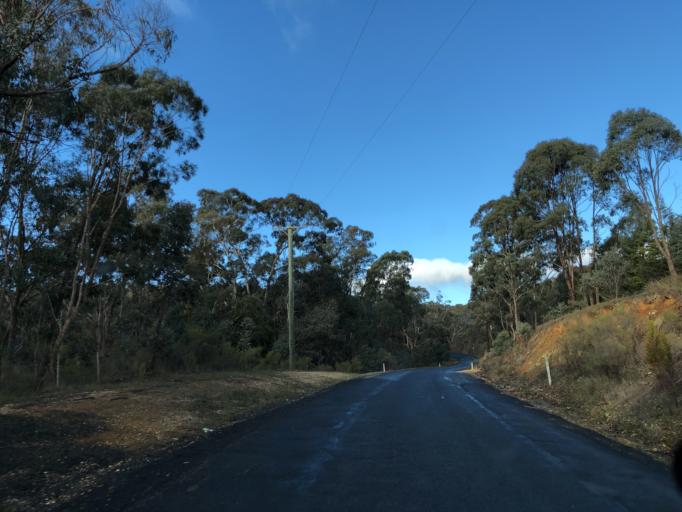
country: AU
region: Victoria
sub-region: Mount Alexander
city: Castlemaine
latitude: -37.2075
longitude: 144.2822
